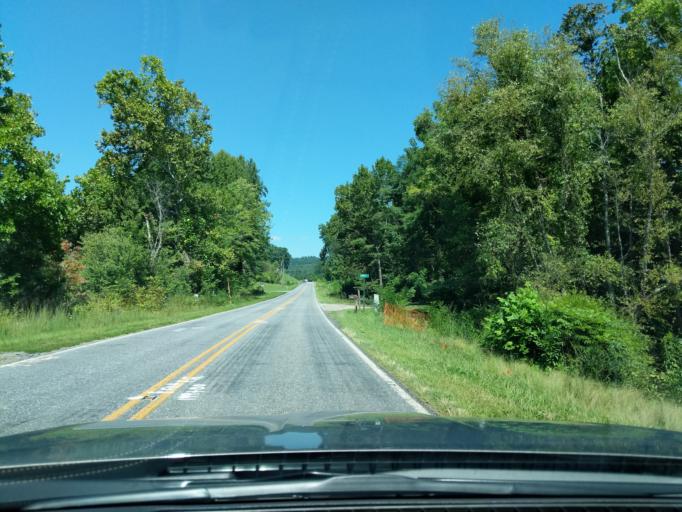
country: US
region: Georgia
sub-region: Towns County
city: Hiawassee
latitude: 35.0271
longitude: -83.7351
